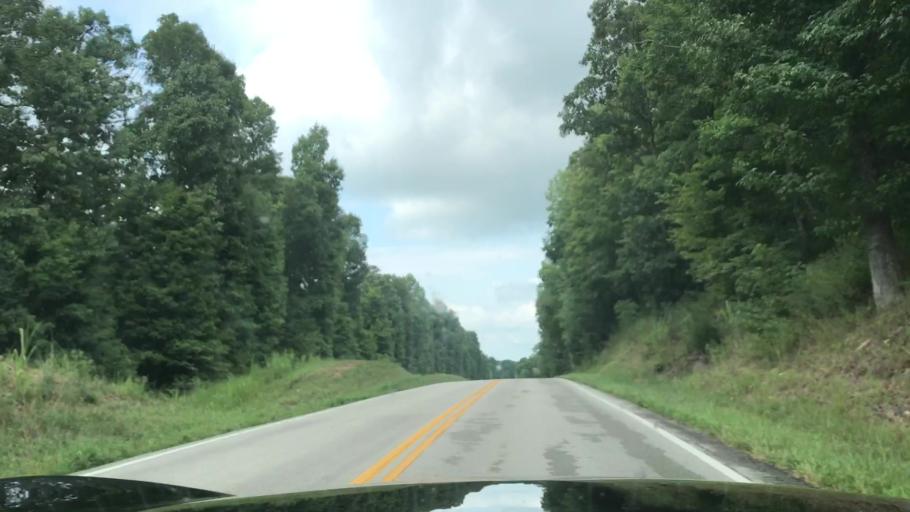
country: US
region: Kentucky
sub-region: Butler County
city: Morgantown
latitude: 37.1724
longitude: -86.8301
